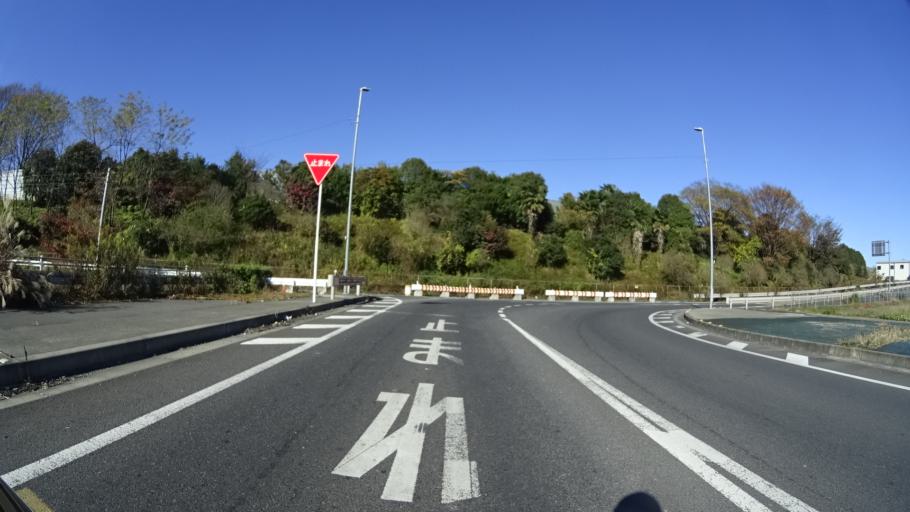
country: JP
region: Tochigi
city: Kanuma
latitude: 36.4960
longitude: 139.7520
